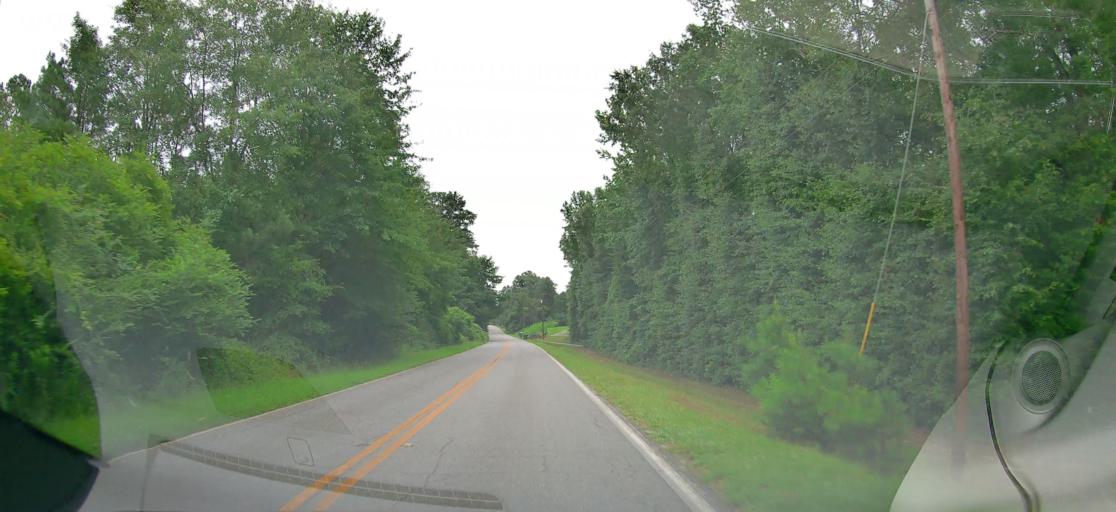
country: US
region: Georgia
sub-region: Bibb County
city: West Point
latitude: 32.7654
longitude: -83.7846
